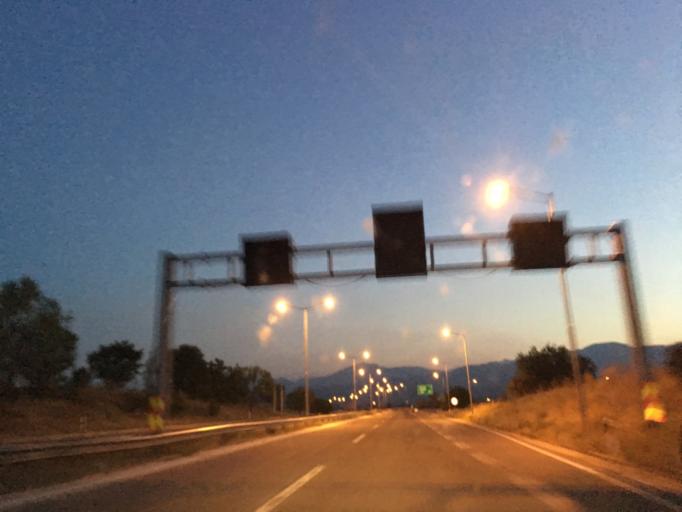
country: MK
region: Petrovec
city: Petrovec
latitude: 41.9424
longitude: 21.6288
